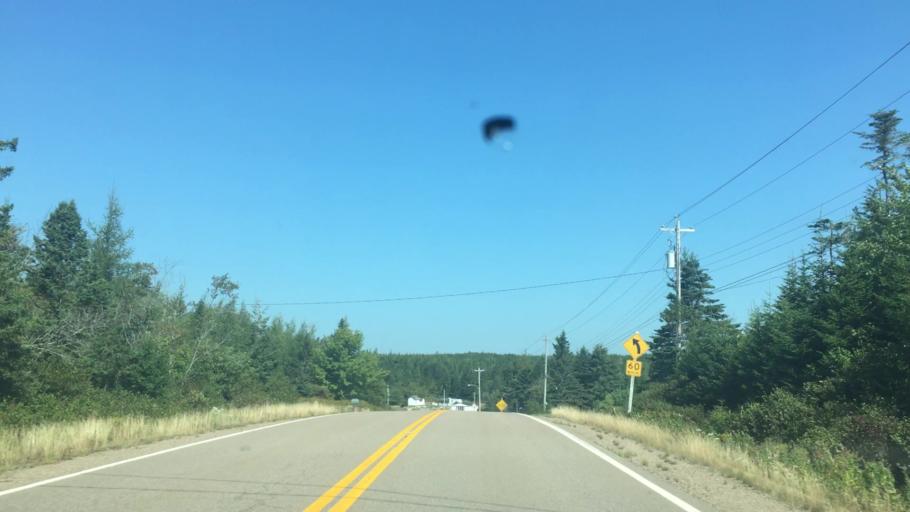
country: CA
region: Nova Scotia
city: Antigonish
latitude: 45.0253
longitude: -62.0312
